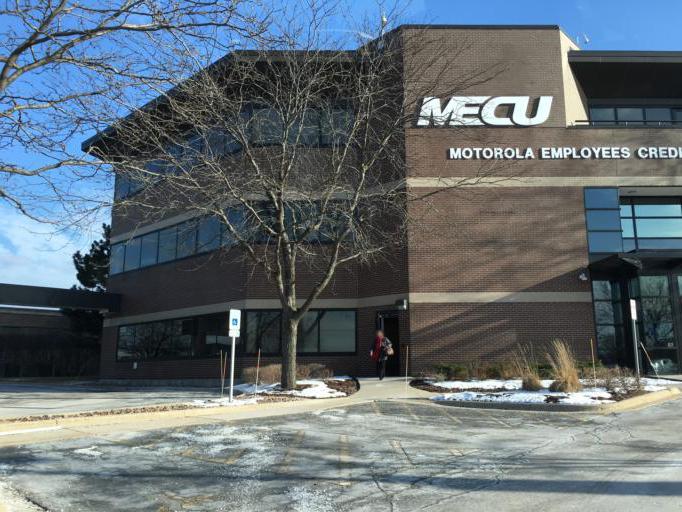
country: US
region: Illinois
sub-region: Cook County
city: Hoffman Estates
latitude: 42.0694
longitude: -88.0550
